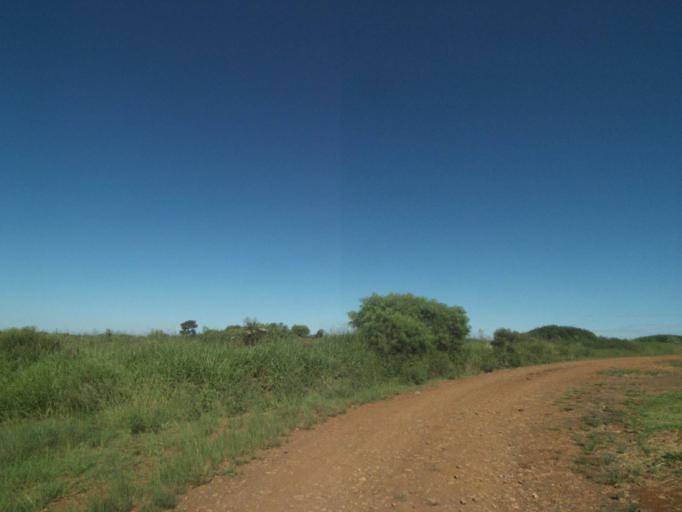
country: BR
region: Parana
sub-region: Pinhao
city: Pinhao
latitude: -25.8362
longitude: -52.0329
